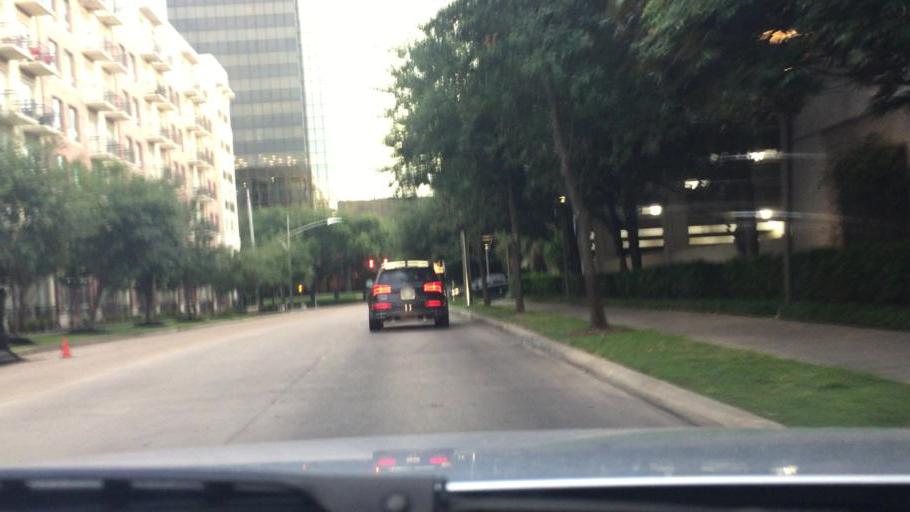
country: US
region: Texas
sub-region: Harris County
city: Bellaire
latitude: 29.7366
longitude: -95.4628
